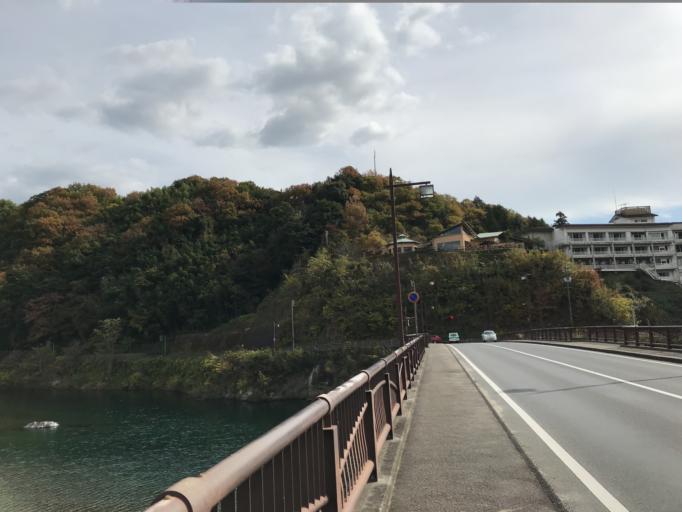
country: JP
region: Yamaguchi
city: Iwakuni
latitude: 34.1696
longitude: 132.1795
